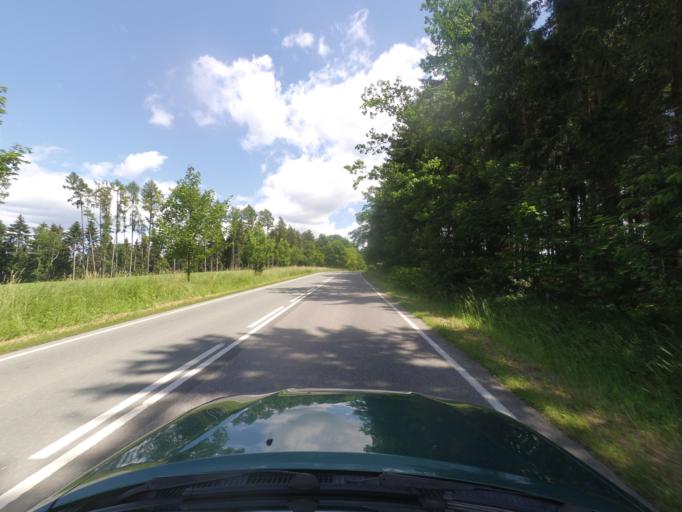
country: CZ
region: Kralovehradecky
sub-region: Okres Rychnov nad Kneznou
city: Rychnov nad Kneznou
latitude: 50.1647
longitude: 16.3123
